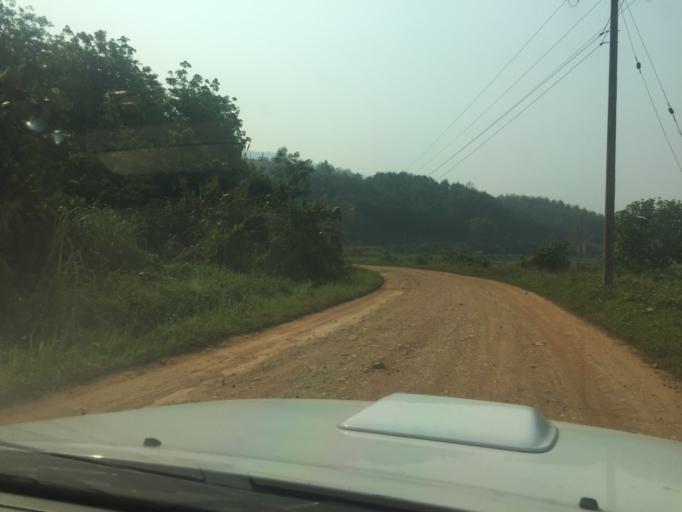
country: TH
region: Phayao
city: Phu Sang
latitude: 19.6673
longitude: 100.5285
